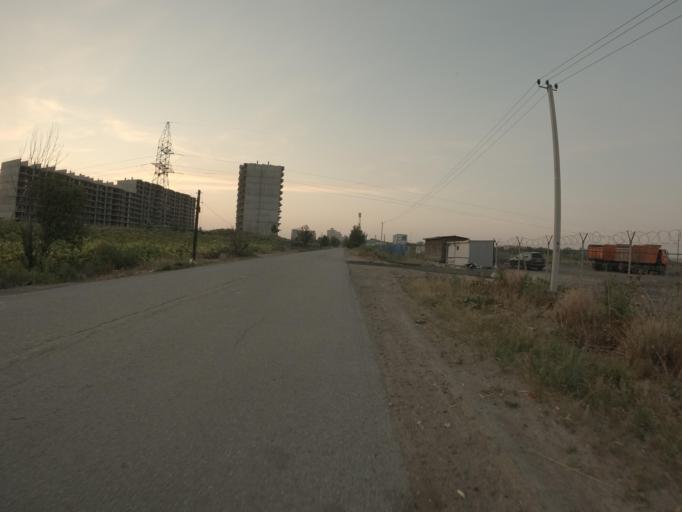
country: RU
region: Leningrad
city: Yanino Vtoroye
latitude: 59.9416
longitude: 30.5530
